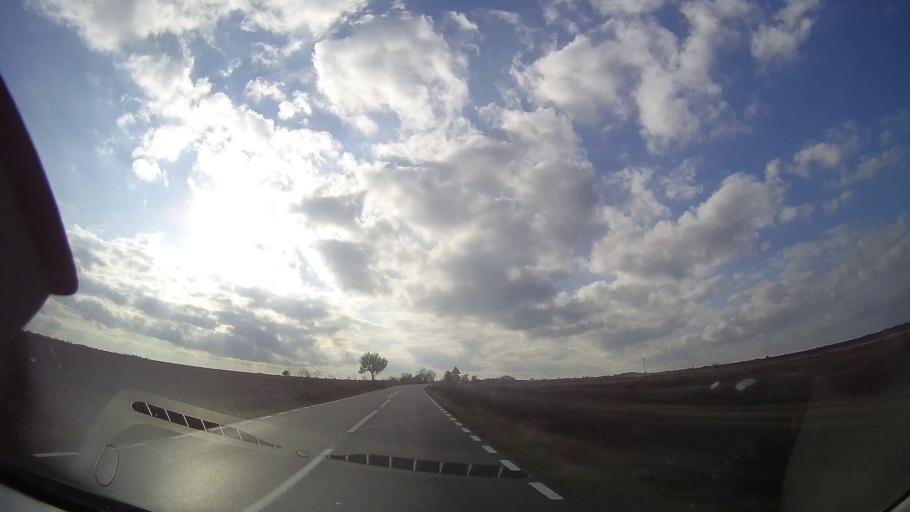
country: RO
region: Constanta
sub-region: Comuna Albesti
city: Albesti
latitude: 43.8159
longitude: 28.4572
